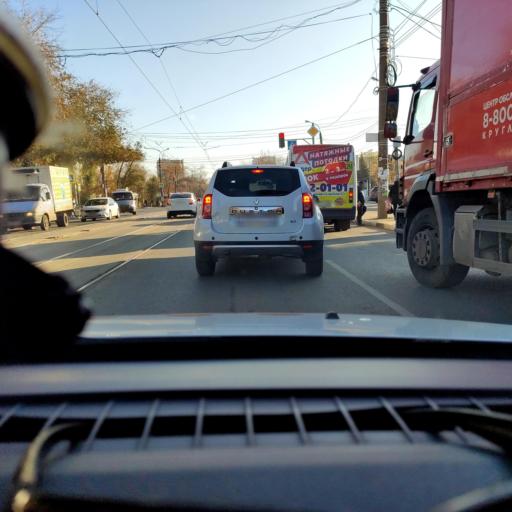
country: RU
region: Samara
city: Samara
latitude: 53.1912
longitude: 50.1779
